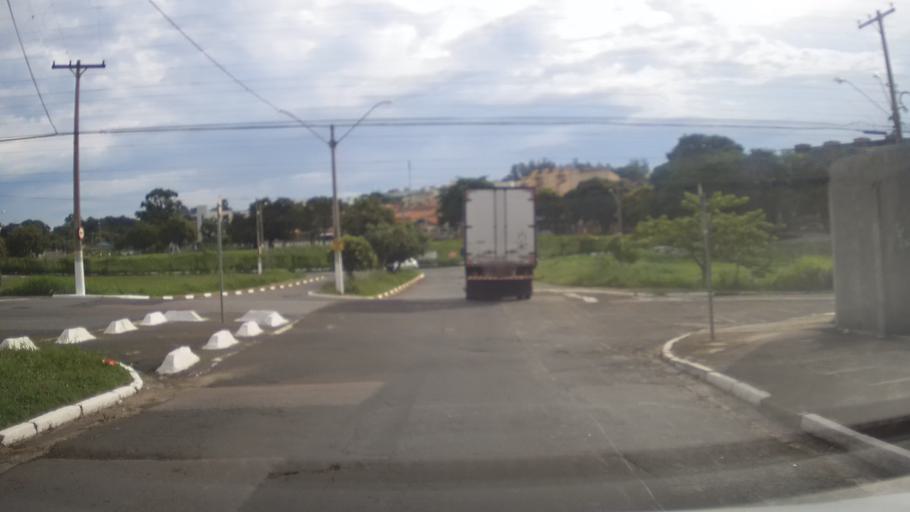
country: BR
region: Sao Paulo
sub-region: Campinas
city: Campinas
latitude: -22.9072
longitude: -47.1138
